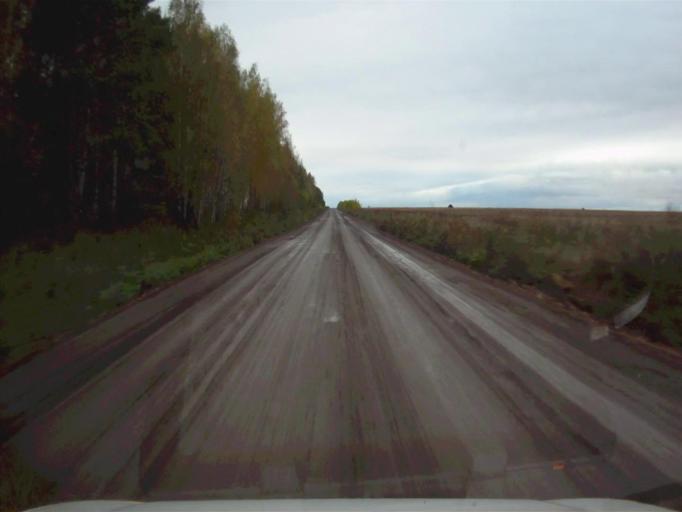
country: RU
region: Sverdlovsk
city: Mikhaylovsk
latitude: 56.1517
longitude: 59.2673
